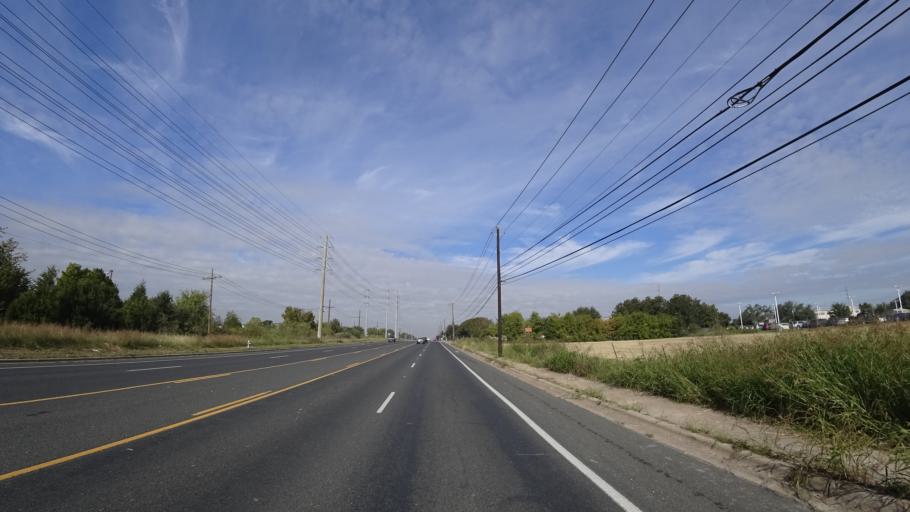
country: US
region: Texas
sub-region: Travis County
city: Austin
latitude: 30.2090
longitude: -97.7236
